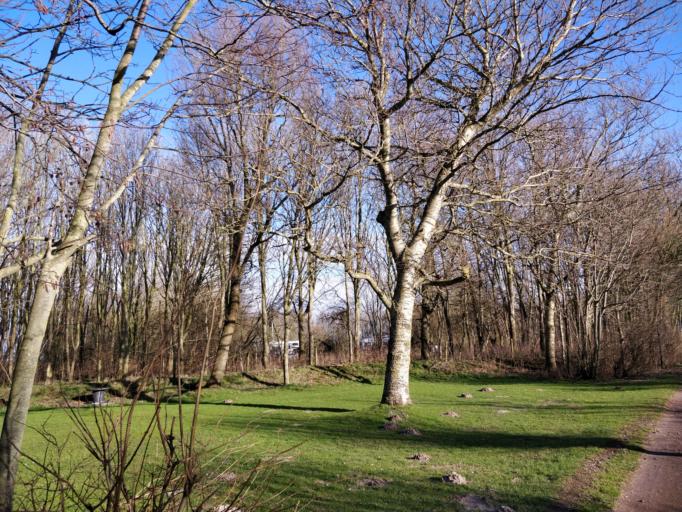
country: NL
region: Friesland
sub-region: Gemeente Het Bildt
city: Sint Annaparochie
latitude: 53.3091
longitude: 5.6286
